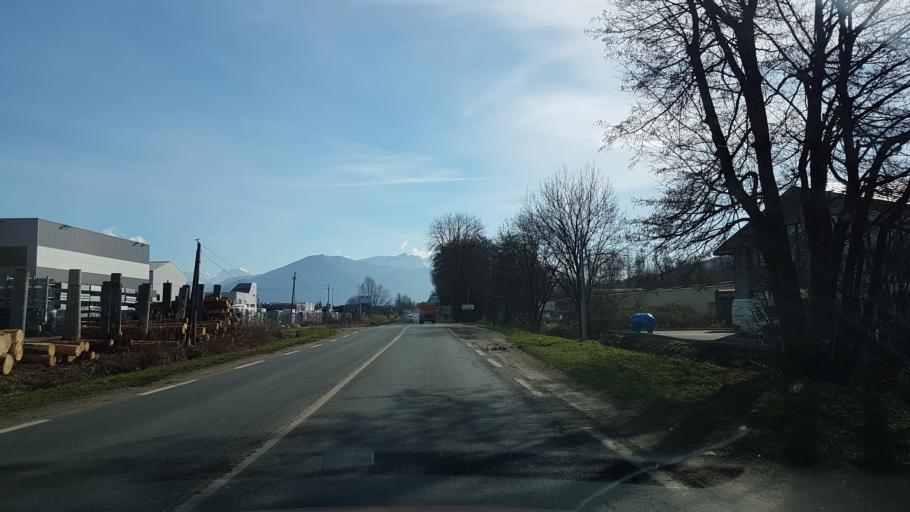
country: FR
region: Rhone-Alpes
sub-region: Departement de la Haute-Savoie
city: Poisy
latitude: 45.9416
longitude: 6.0630
